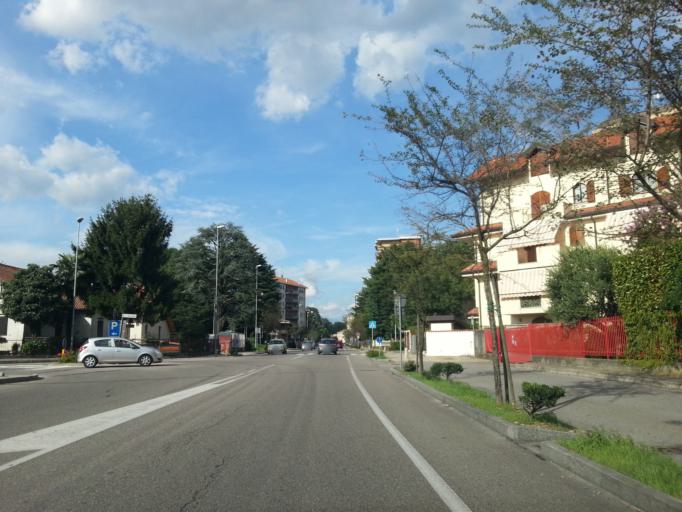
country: IT
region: Lombardy
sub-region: Provincia di Monza e Brianza
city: Vedano al Lambro
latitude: 45.6072
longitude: 9.2684
